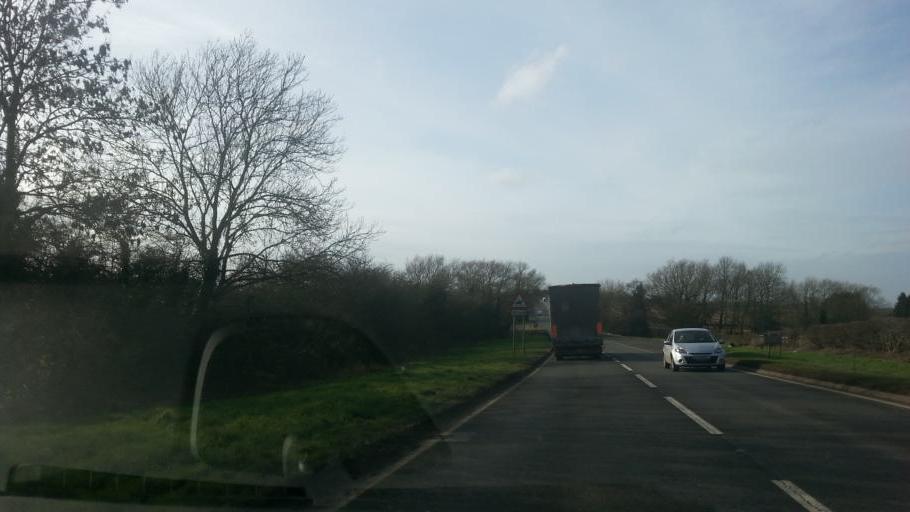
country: GB
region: England
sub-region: District of Rutland
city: Ridlington
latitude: 52.5959
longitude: -0.8162
